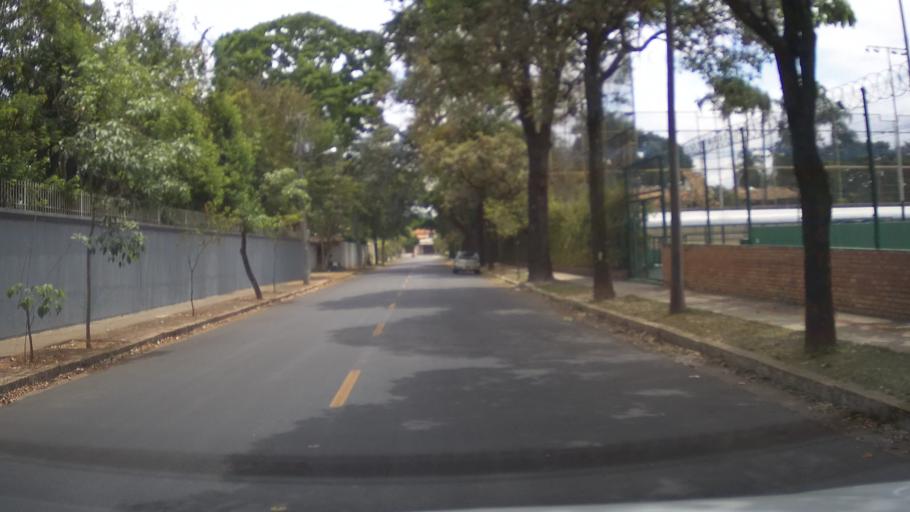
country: BR
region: Minas Gerais
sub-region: Belo Horizonte
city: Belo Horizonte
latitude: -19.8561
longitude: -43.9734
